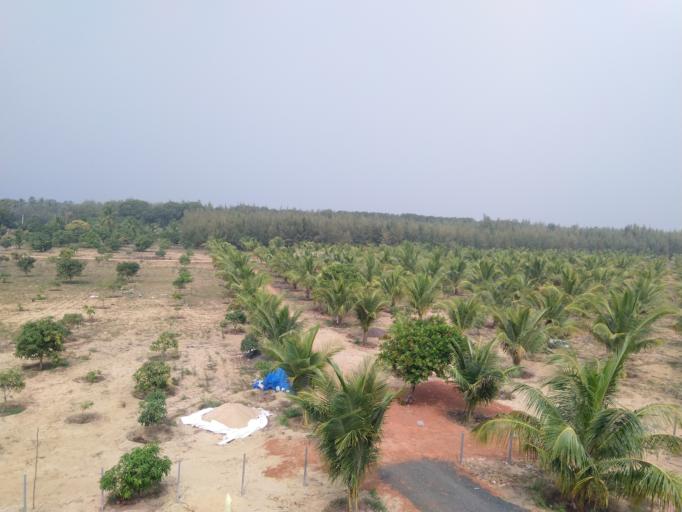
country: IN
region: Andhra Pradesh
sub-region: West Godavari
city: Bhimavaram
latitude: 16.3582
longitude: 81.4511
